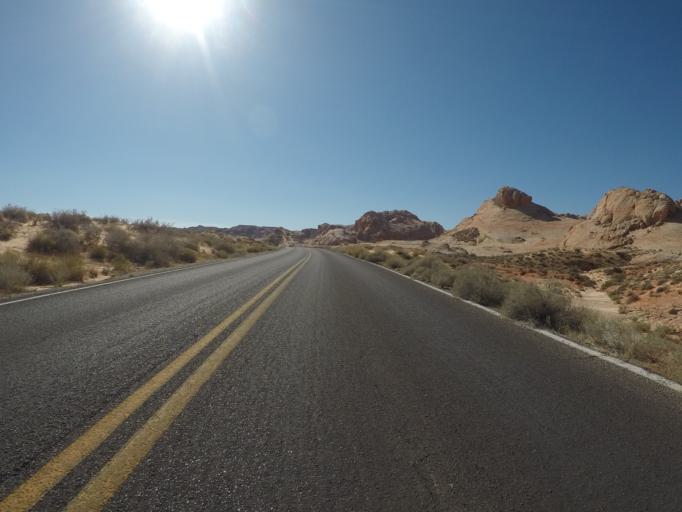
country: US
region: Nevada
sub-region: Clark County
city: Moapa Valley
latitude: 36.4779
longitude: -114.5272
